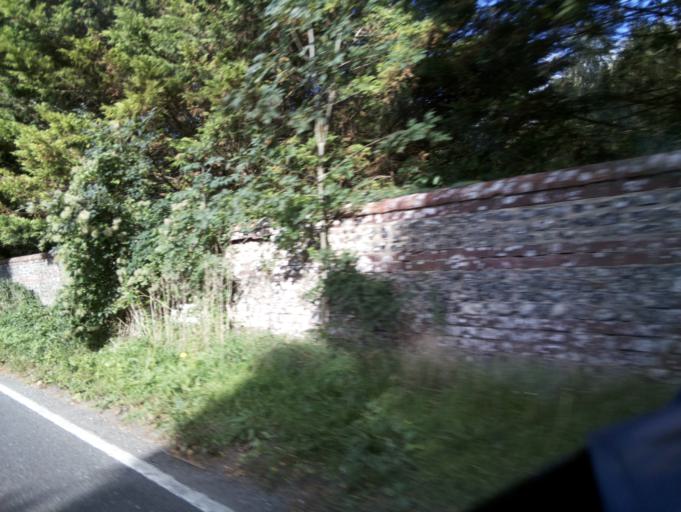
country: GB
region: England
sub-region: Hampshire
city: Basingstoke
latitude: 51.2384
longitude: -1.0788
